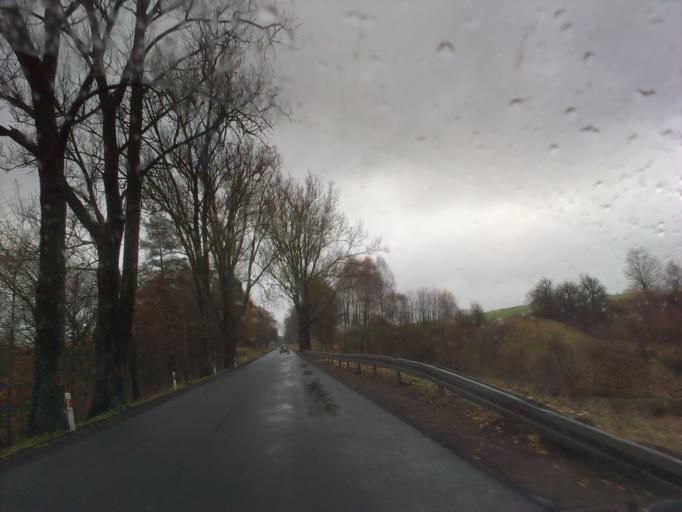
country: PL
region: West Pomeranian Voivodeship
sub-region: Powiat szczecinecki
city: Borne Sulinowo
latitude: 53.6238
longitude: 16.4717
